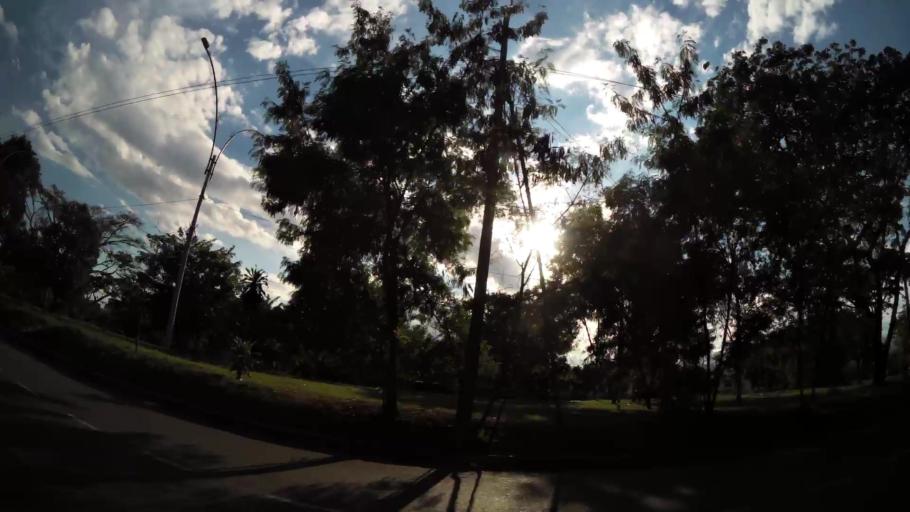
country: CO
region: Valle del Cauca
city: Cali
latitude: 3.4744
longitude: -76.4870
